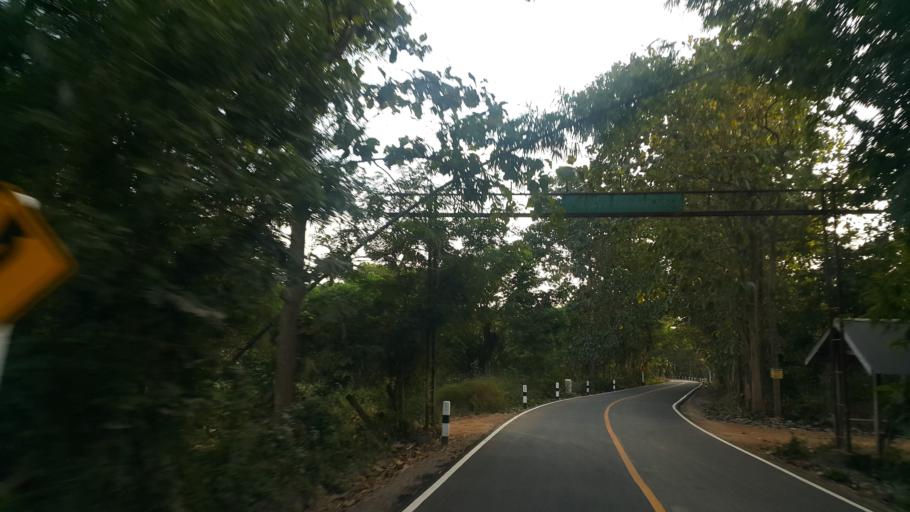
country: TH
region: Lampang
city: Sop Prap
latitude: 17.9383
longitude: 99.3409
